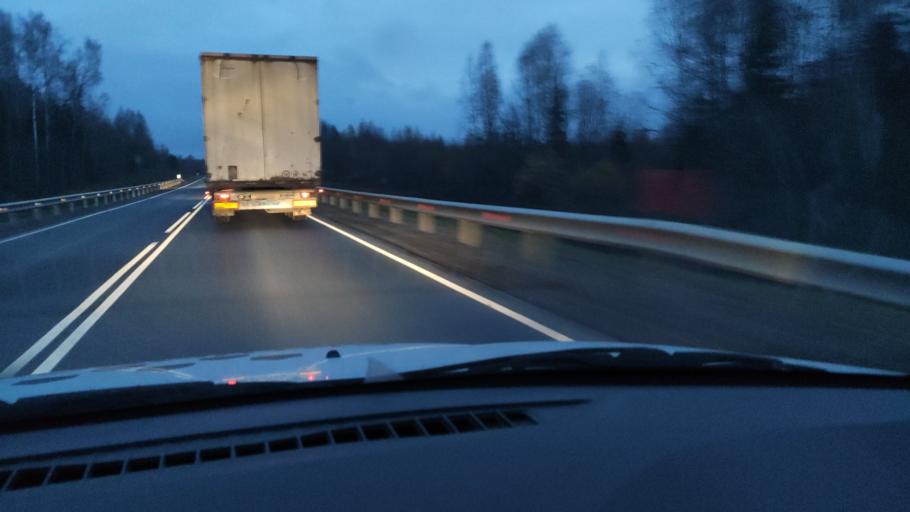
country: RU
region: Kirov
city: Kostino
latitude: 58.8336
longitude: 53.4837
